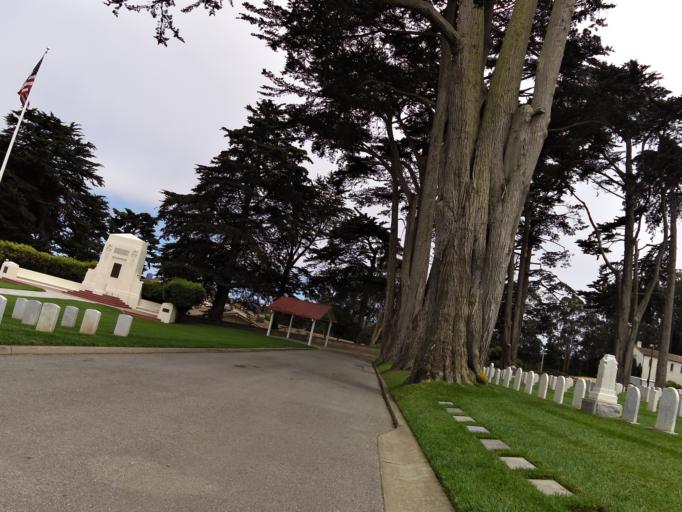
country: US
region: California
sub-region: San Francisco County
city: San Francisco
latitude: 37.8008
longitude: -122.4627
